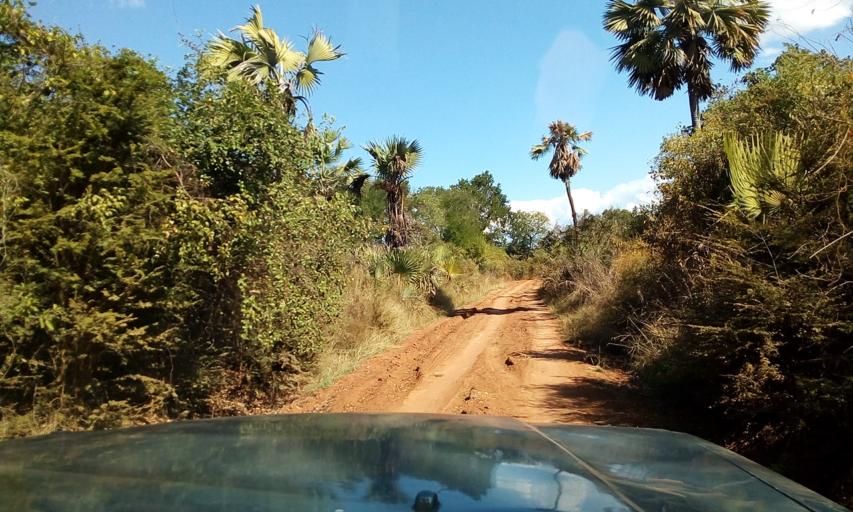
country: MG
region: Boeny
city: Mahajanga
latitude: -16.0539
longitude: 45.8105
